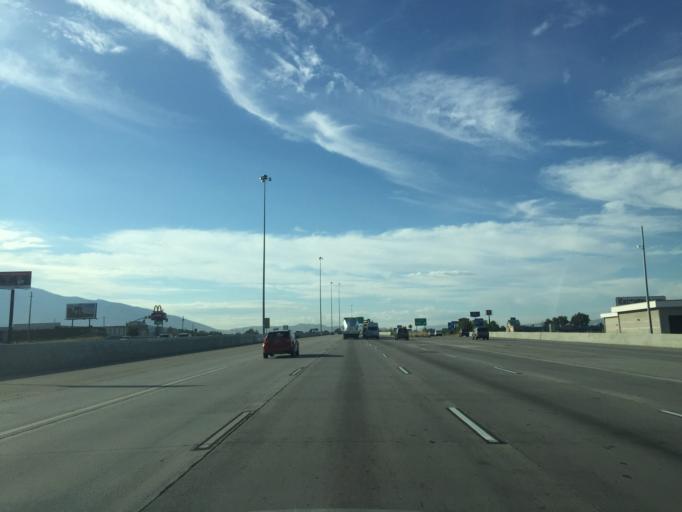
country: US
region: Utah
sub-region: Salt Lake County
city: Centerfield
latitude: 40.6790
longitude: -111.9022
